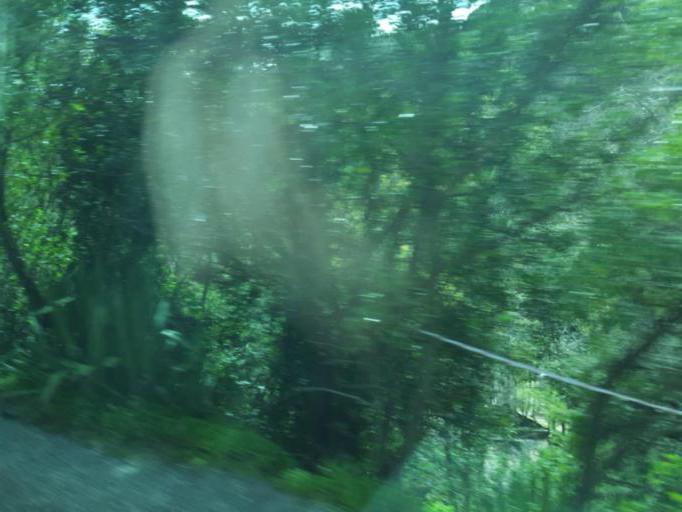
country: PT
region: Faro
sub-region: Monchique
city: Monchique
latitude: 37.2874
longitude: -8.5541
